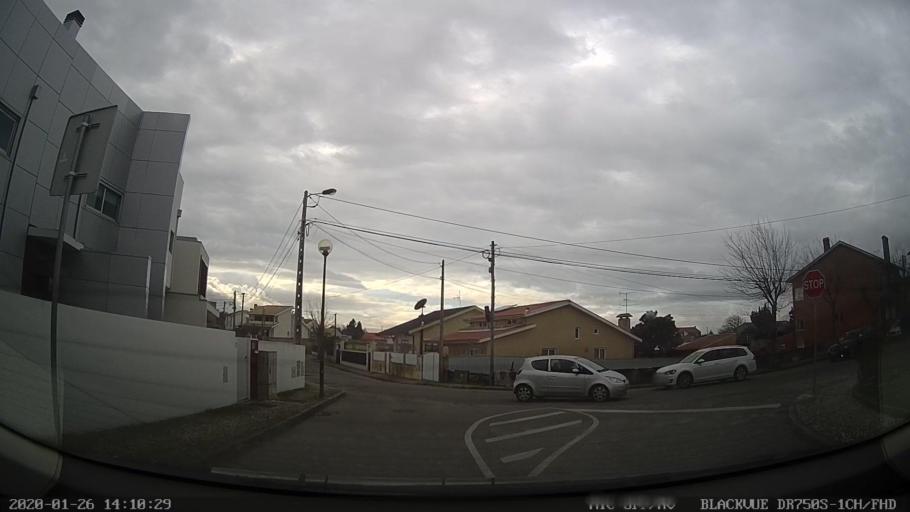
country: PT
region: Aveiro
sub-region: Aveiro
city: Aradas
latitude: 40.6294
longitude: -8.6281
